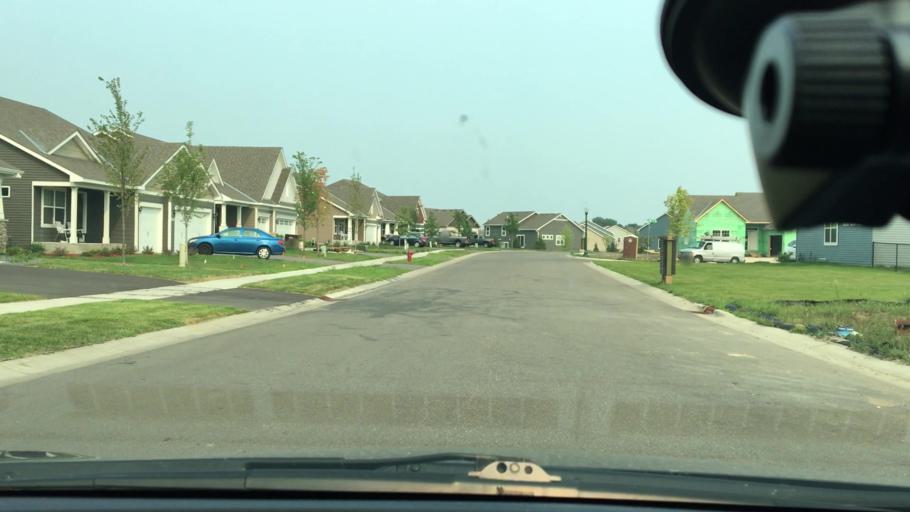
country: US
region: Minnesota
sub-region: Hennepin County
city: Champlin
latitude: 45.1984
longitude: -93.4374
